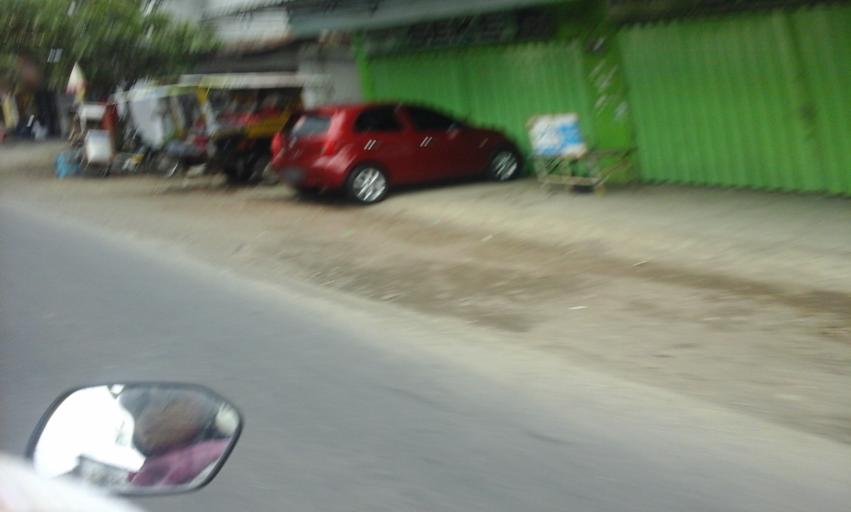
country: ID
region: East Java
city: Jenggawah
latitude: -8.2610
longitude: 113.6501
